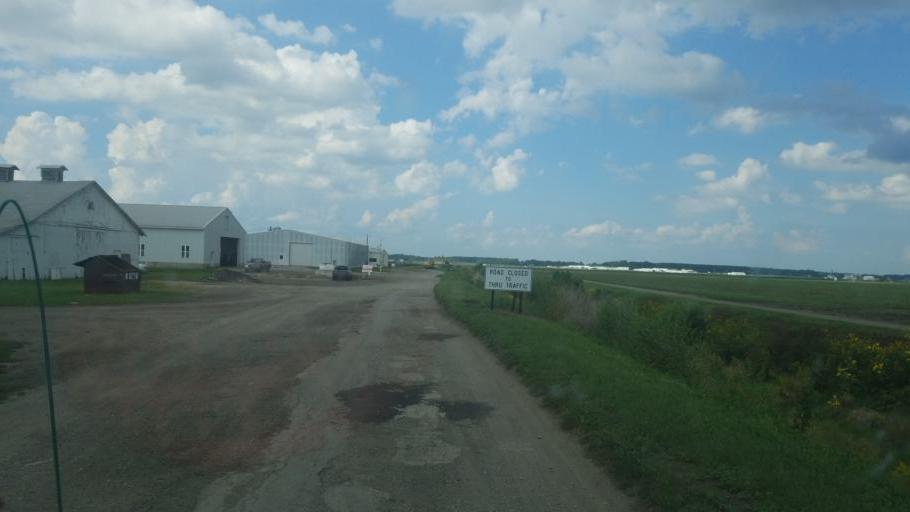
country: US
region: Ohio
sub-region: Huron County
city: Willard
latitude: 41.0045
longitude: -82.7393
